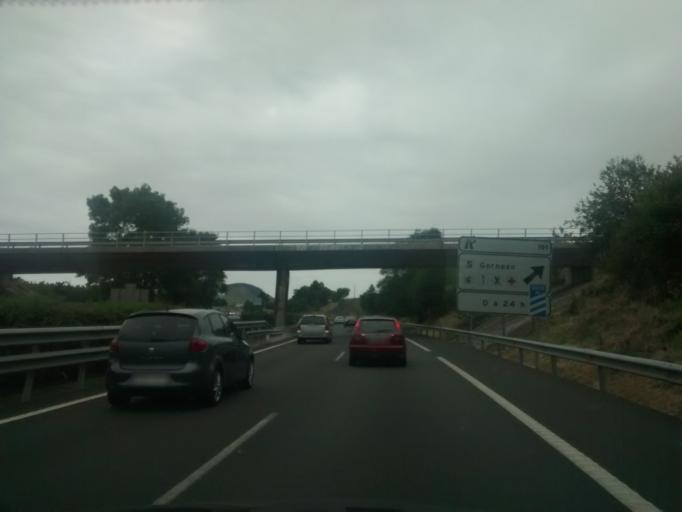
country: ES
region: Cantabria
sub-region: Provincia de Cantabria
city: Miengo
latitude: 43.4010
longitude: -3.9929
